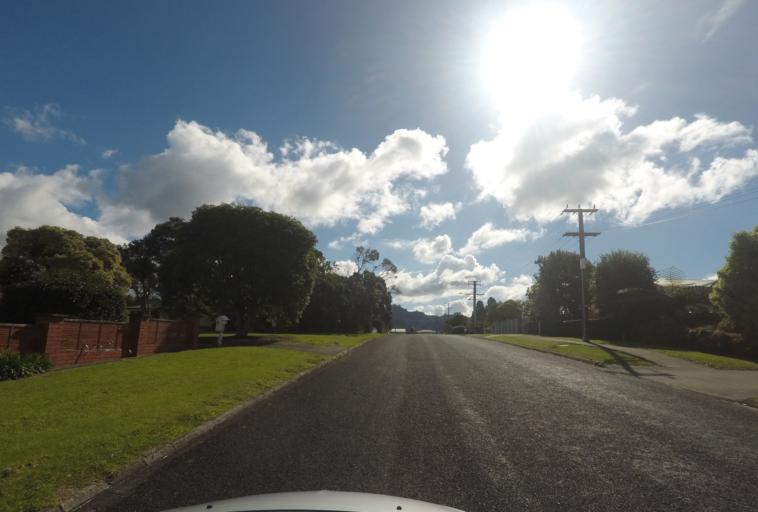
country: NZ
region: Bay of Plenty
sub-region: Western Bay of Plenty District
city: Waihi Beach
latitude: -37.4138
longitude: 175.9390
